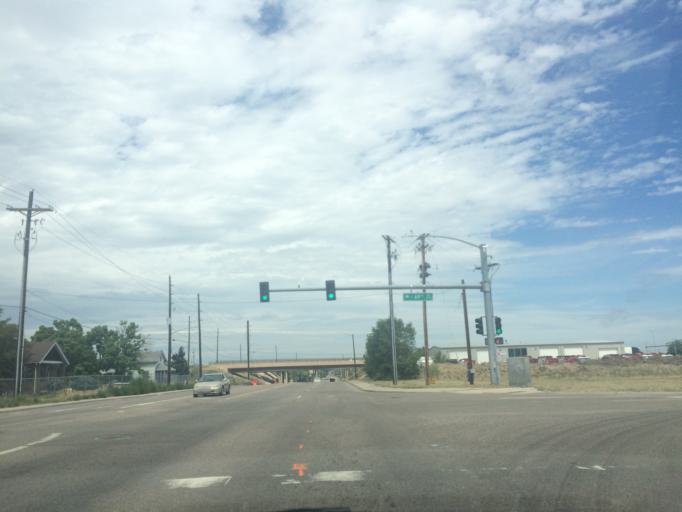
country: US
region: Colorado
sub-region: Adams County
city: Welby
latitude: 39.8220
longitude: -104.9591
